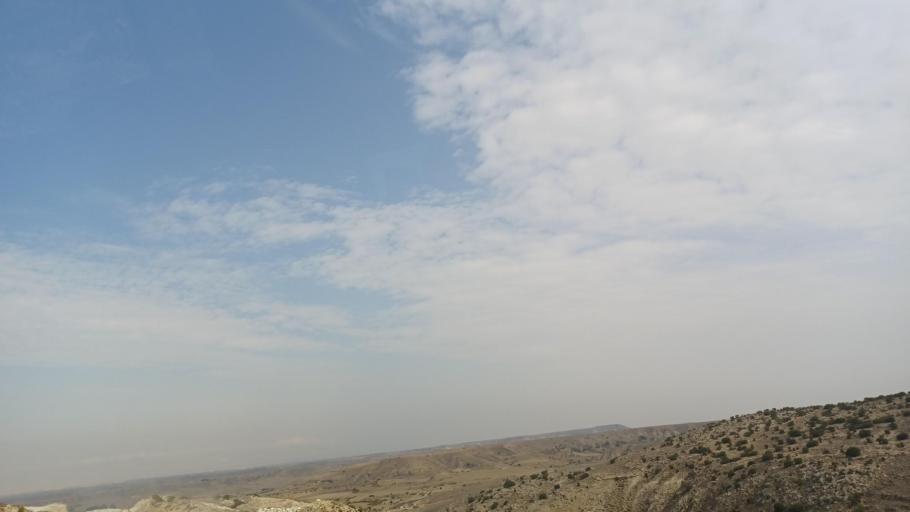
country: CY
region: Lefkosia
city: Meniko
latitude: 35.0562
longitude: 33.1279
